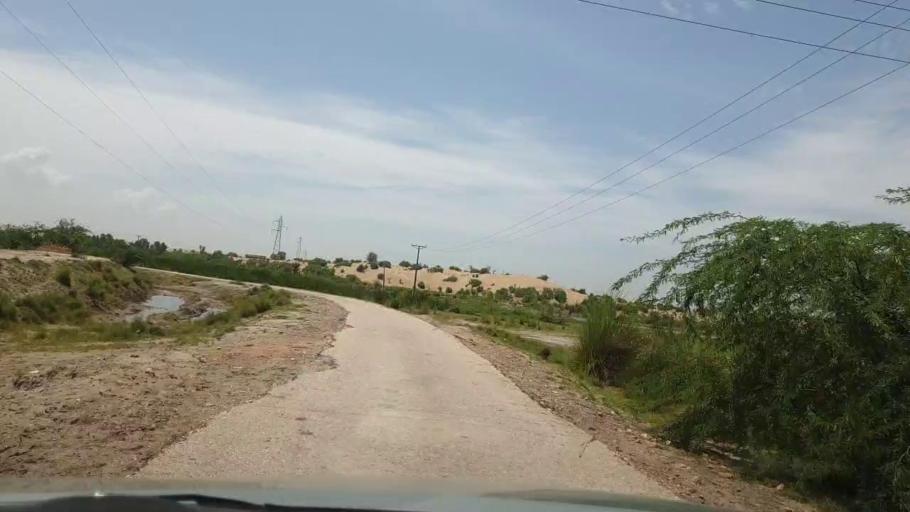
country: PK
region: Sindh
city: Bozdar
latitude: 27.0796
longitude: 68.9661
